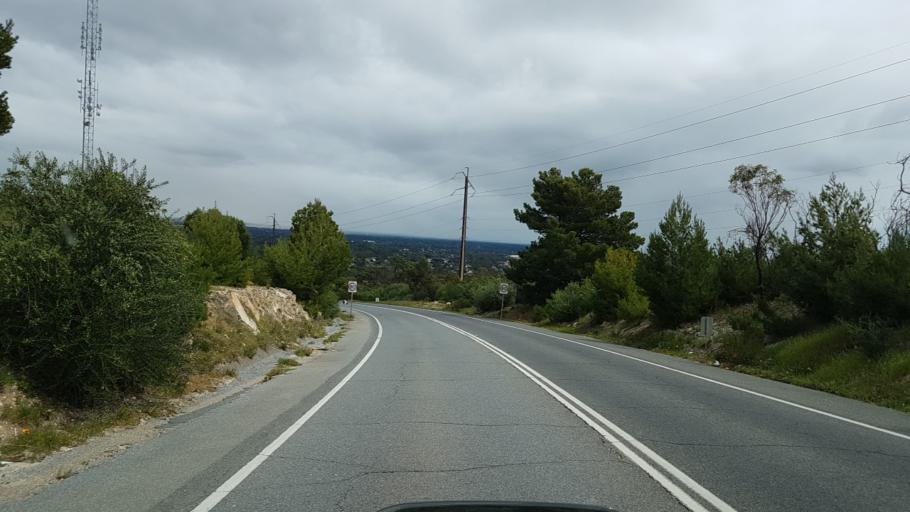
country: AU
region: South Australia
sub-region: Salisbury
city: Elizabeth
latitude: -34.7433
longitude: 138.6902
